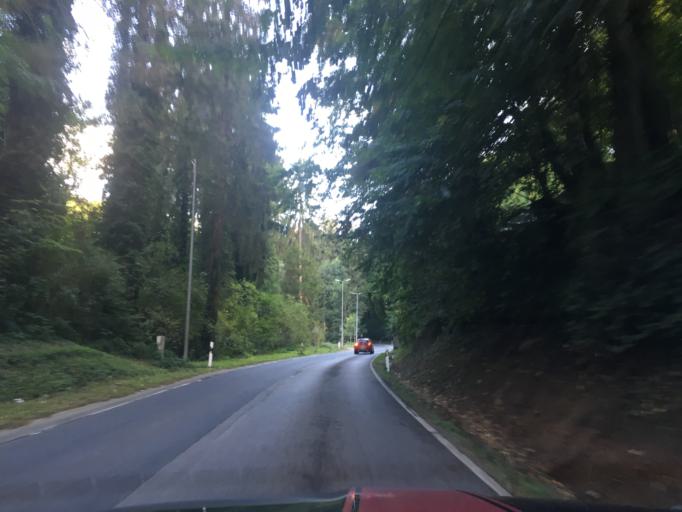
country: LU
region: Luxembourg
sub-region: Canton d'Esch-sur-Alzette
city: Differdange
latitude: 49.5133
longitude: 5.8724
